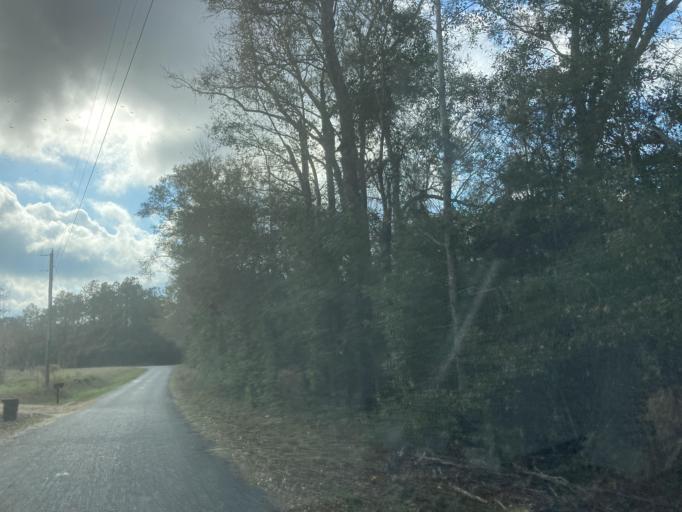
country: US
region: Mississippi
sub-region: Stone County
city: Wiggins
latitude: 30.8008
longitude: -89.1075
